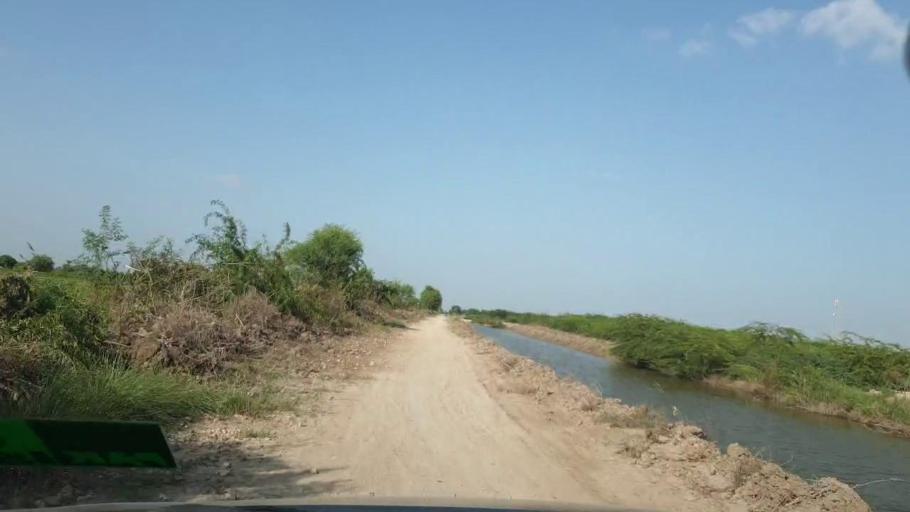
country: PK
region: Sindh
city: Naukot
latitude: 24.7080
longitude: 69.2042
